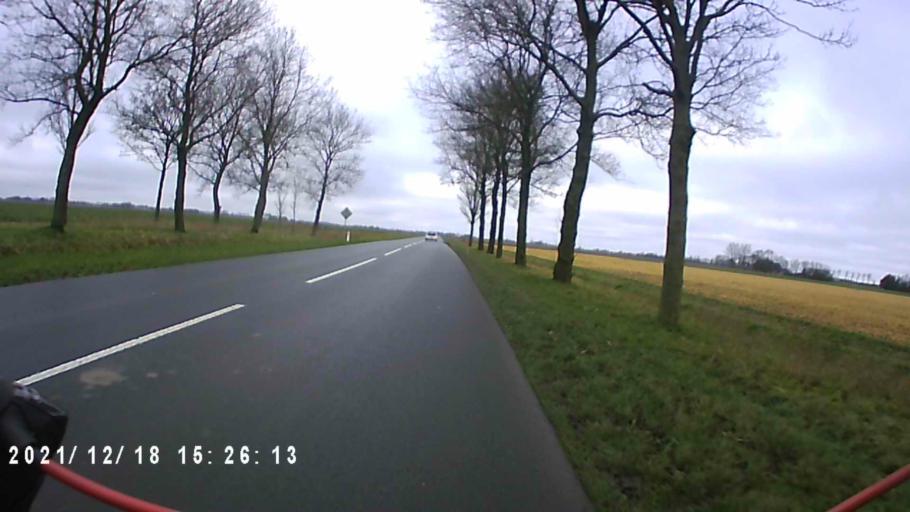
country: NL
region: Friesland
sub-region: Gemeente Kollumerland en Nieuwkruisland
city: Kollum
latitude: 53.3265
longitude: 6.1505
